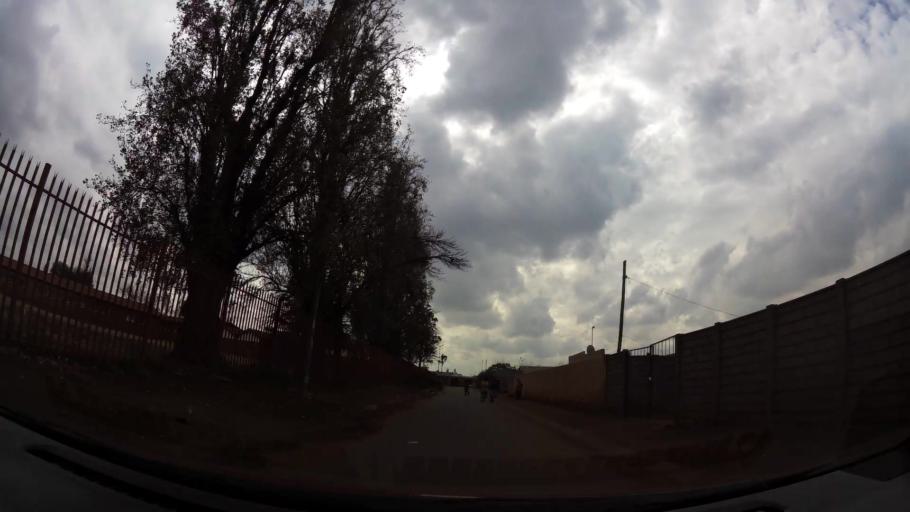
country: ZA
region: Gauteng
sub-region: City of Johannesburg Metropolitan Municipality
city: Soweto
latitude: -26.2574
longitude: 27.8342
